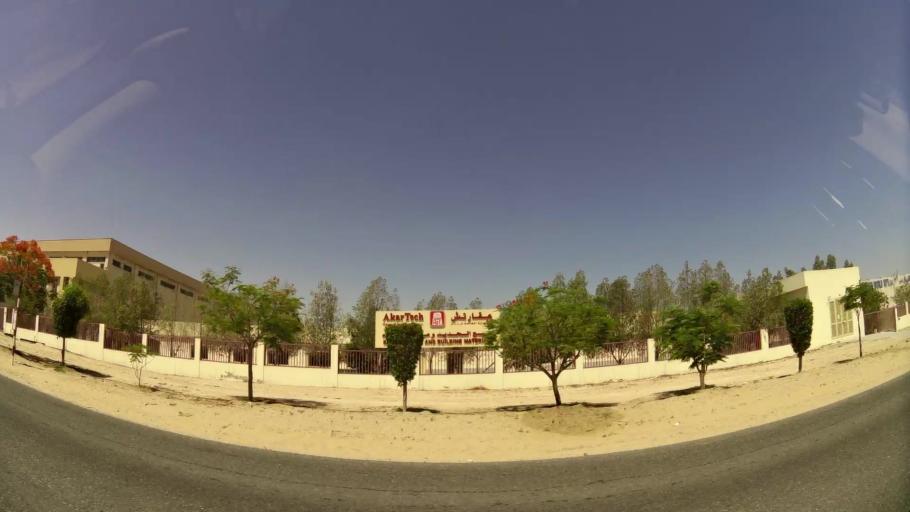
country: AE
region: Dubai
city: Dubai
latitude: 24.9816
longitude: 55.2075
